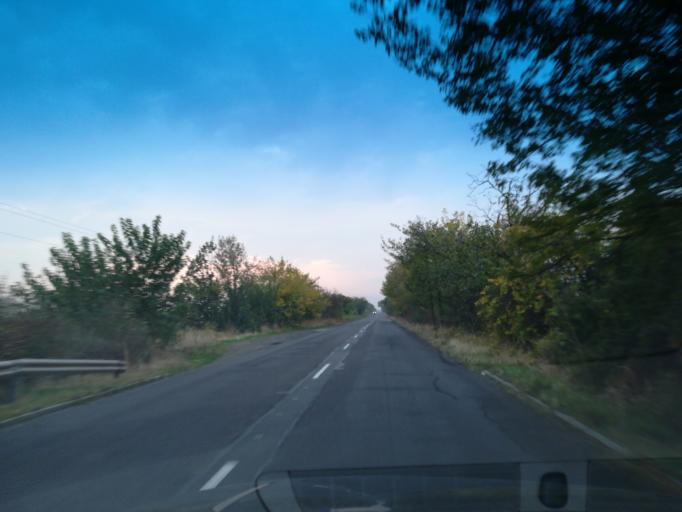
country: BG
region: Stara Zagora
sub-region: Obshtina Chirpan
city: Chirpan
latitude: 42.1900
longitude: 25.2850
